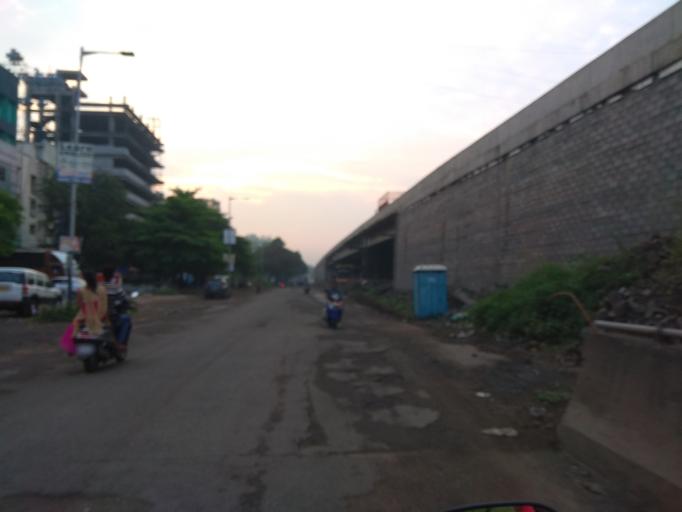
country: IN
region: Maharashtra
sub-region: Pune Division
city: Kharakvasla
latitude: 18.4852
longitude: 73.7990
